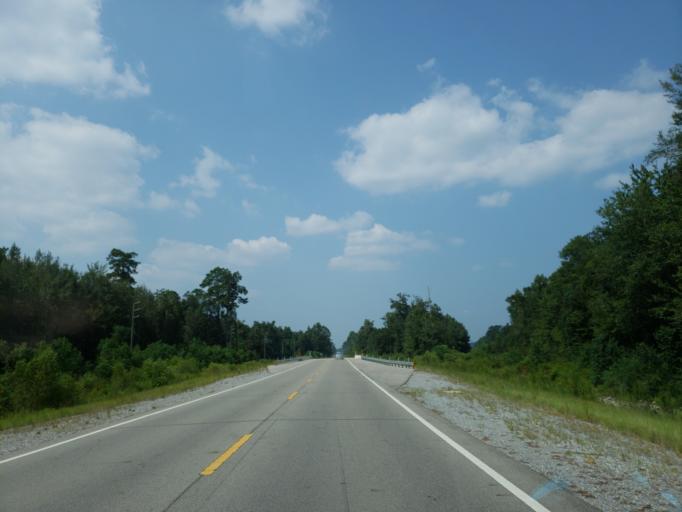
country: US
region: Mississippi
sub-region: Forrest County
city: Glendale
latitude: 31.4645
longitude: -89.2841
